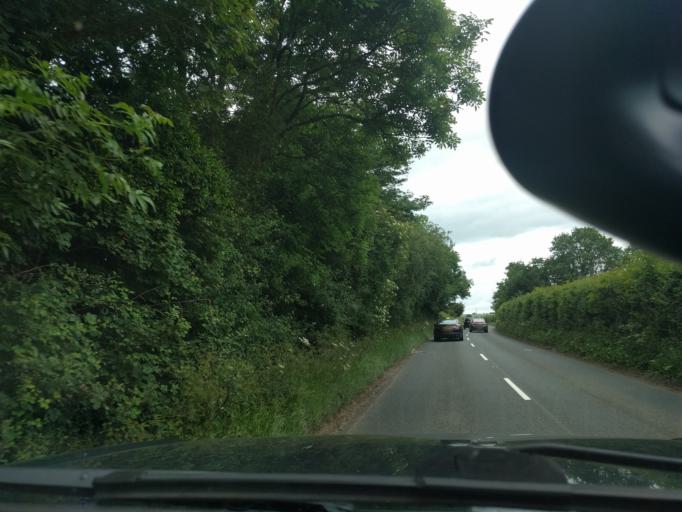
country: GB
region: England
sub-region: Wiltshire
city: Box
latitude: 51.3832
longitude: -2.2351
